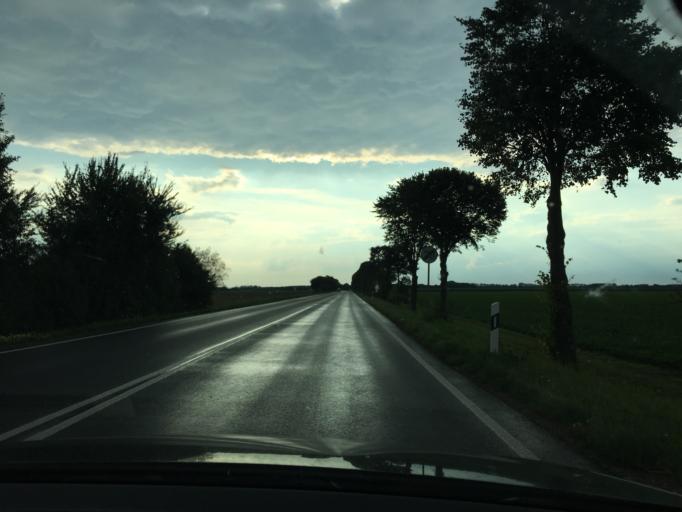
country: DE
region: North Rhine-Westphalia
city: Tuernich
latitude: 50.8246
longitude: 6.7203
